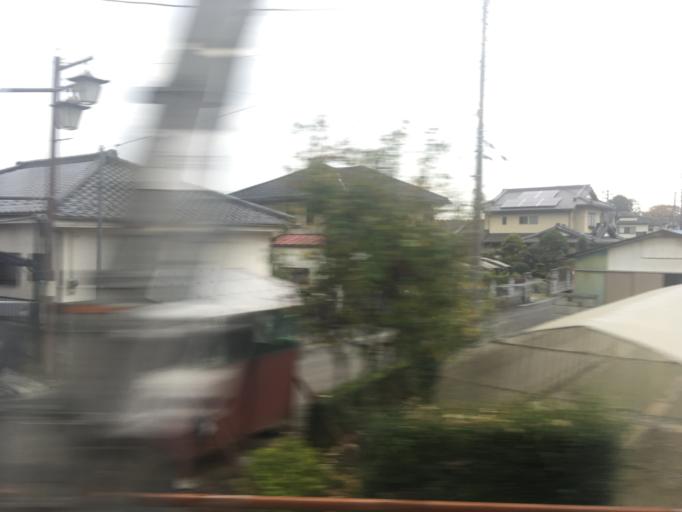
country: JP
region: Saitama
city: Hanno
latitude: 35.8638
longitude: 139.3313
